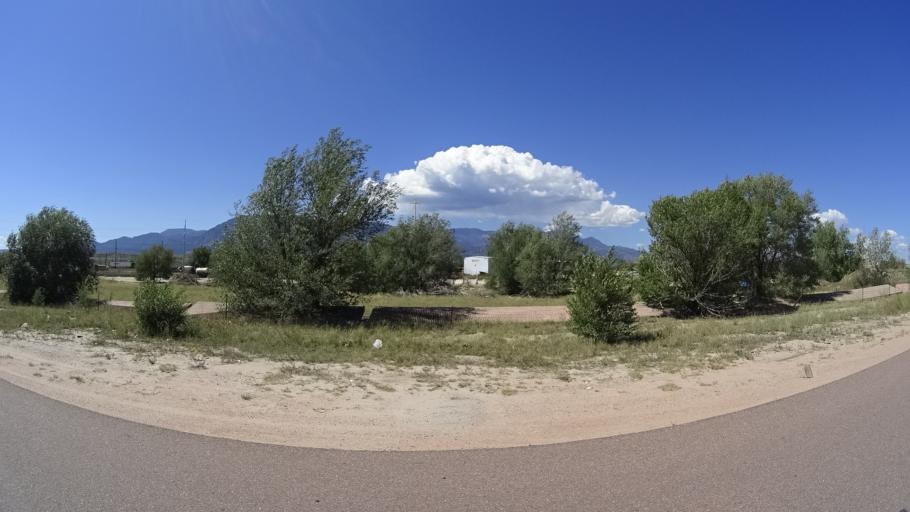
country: US
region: Colorado
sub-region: El Paso County
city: Stratmoor
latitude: 38.7718
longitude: -104.7588
